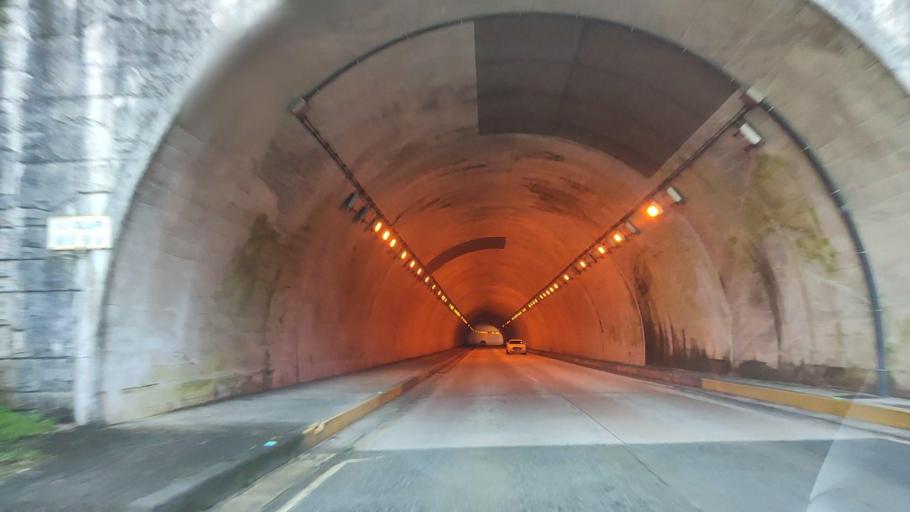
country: JP
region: Ishikawa
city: Nanao
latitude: 37.3845
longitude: 137.2332
